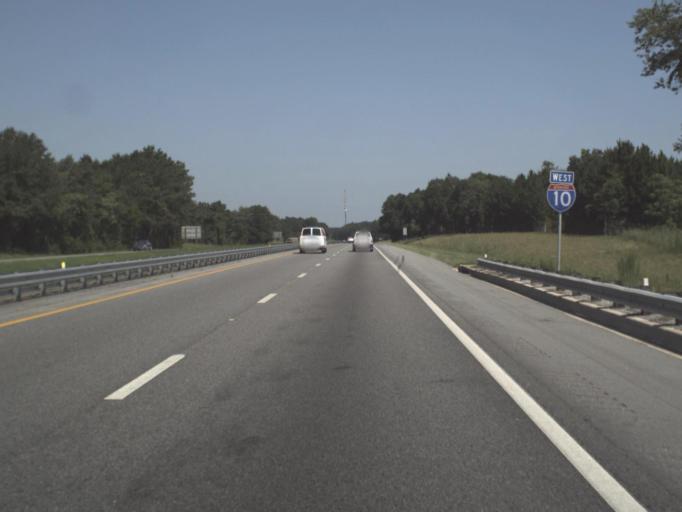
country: US
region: Florida
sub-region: Suwannee County
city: Live Oak
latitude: 30.3356
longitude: -82.9692
